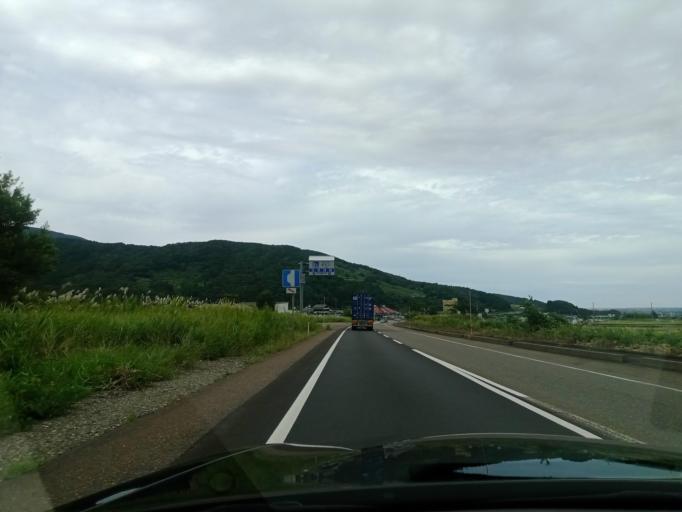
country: JP
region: Niigata
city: Arai
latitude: 37.0213
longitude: 138.2272
